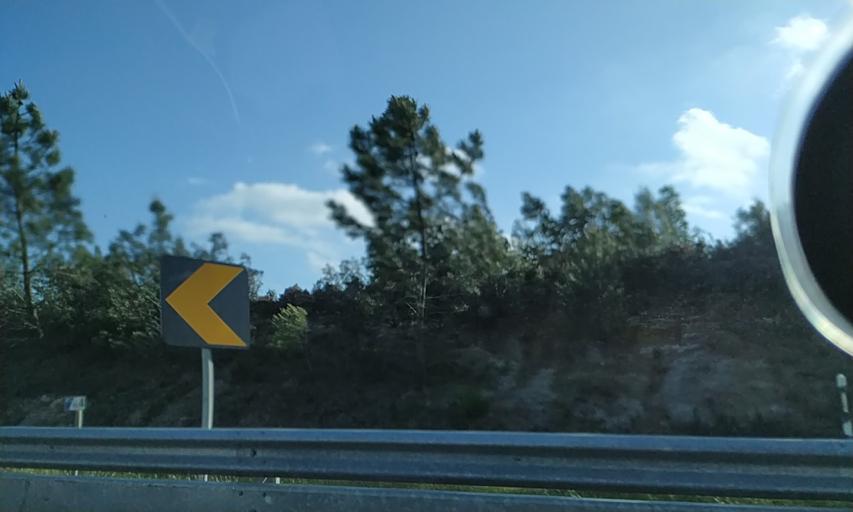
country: PT
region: Lisbon
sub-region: Torres Vedras
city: Torres Vedras
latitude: 39.1166
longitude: -9.2544
